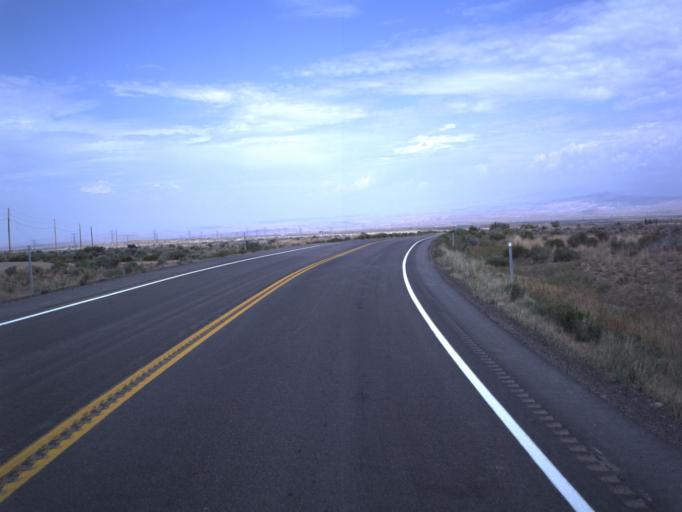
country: US
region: Utah
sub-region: Uintah County
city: Naples
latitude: 40.2035
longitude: -109.3557
